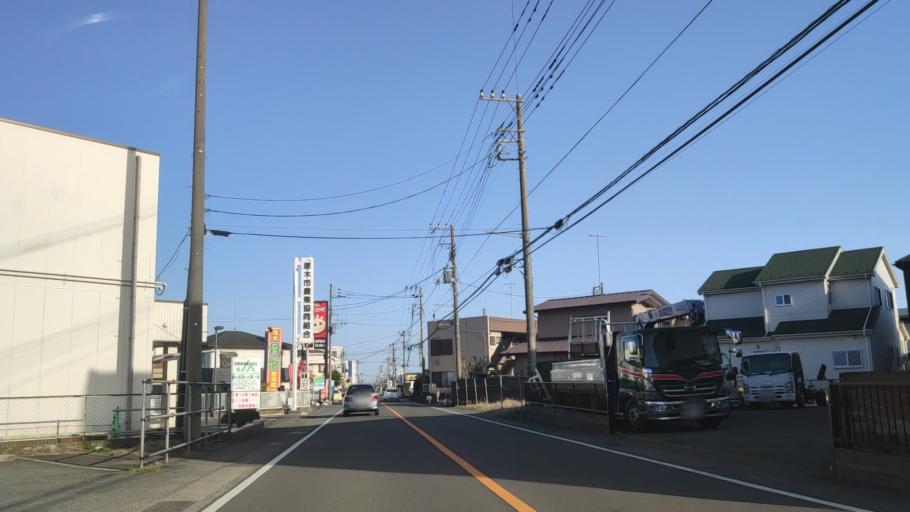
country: JP
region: Kanagawa
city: Zama
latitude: 35.5028
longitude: 139.3542
